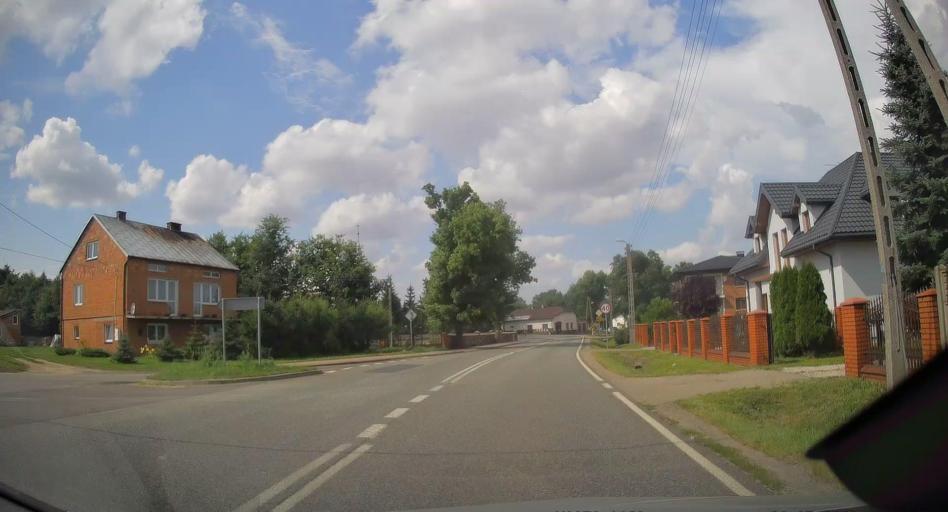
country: PL
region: Lodz Voivodeship
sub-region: Powiat brzezinski
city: Jezow
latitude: 51.8071
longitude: 20.0134
